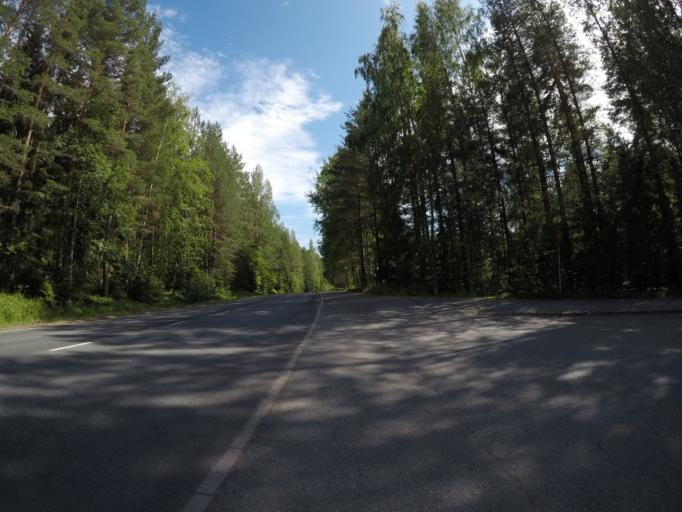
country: FI
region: Haeme
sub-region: Haemeenlinna
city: Haemeenlinna
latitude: 60.9925
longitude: 24.4054
